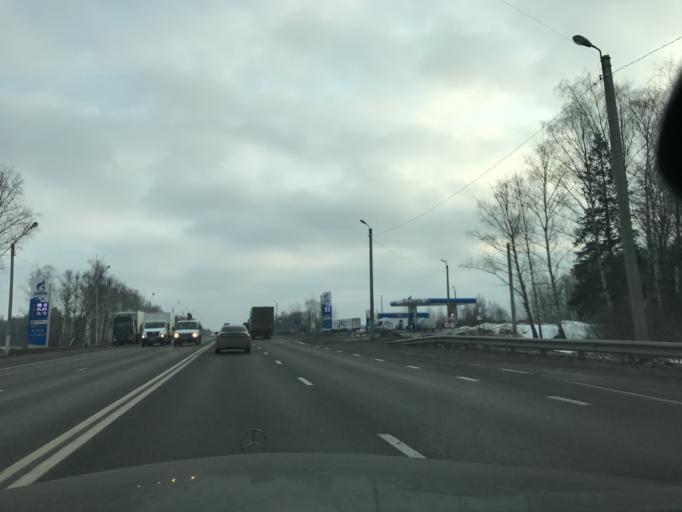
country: RU
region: Vladimir
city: Lakinsk
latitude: 55.9672
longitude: 39.7836
